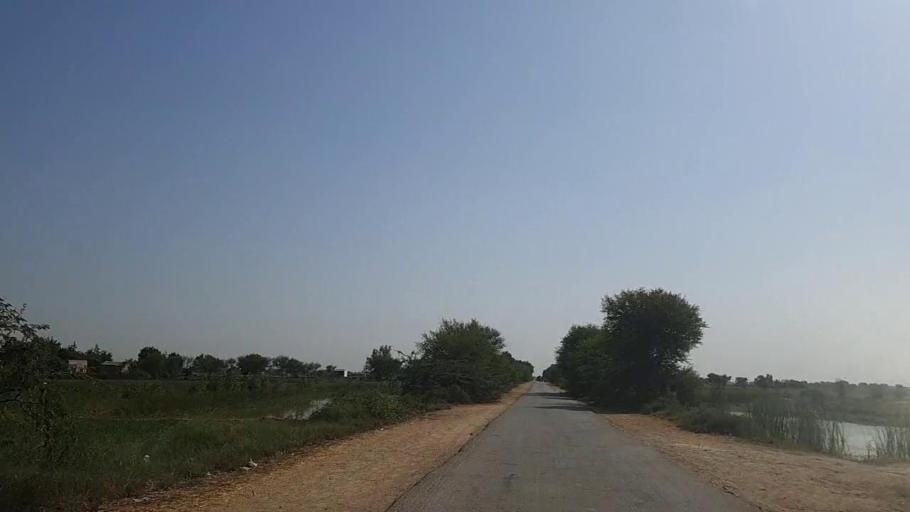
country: PK
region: Sindh
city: Mirpur Batoro
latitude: 24.6566
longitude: 68.2871
